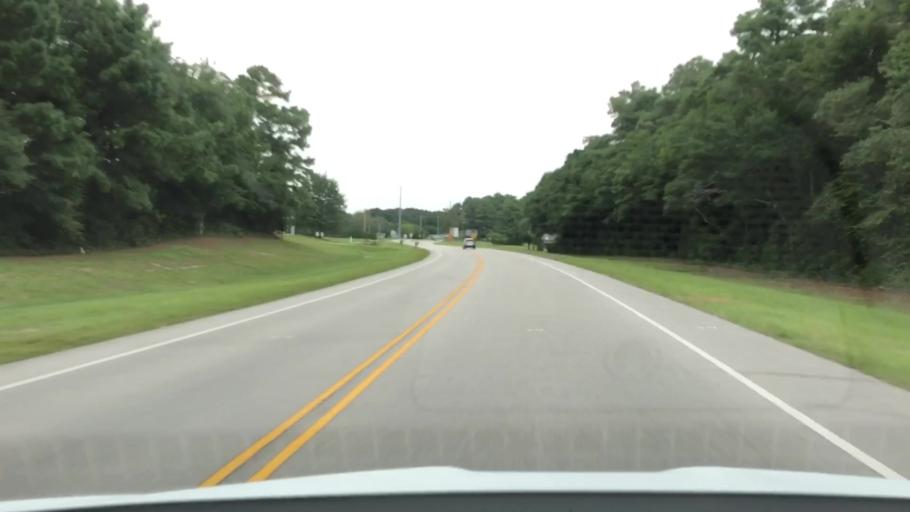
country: US
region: North Carolina
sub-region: Carteret County
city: Cape Carteret
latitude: 34.7030
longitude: -77.0676
